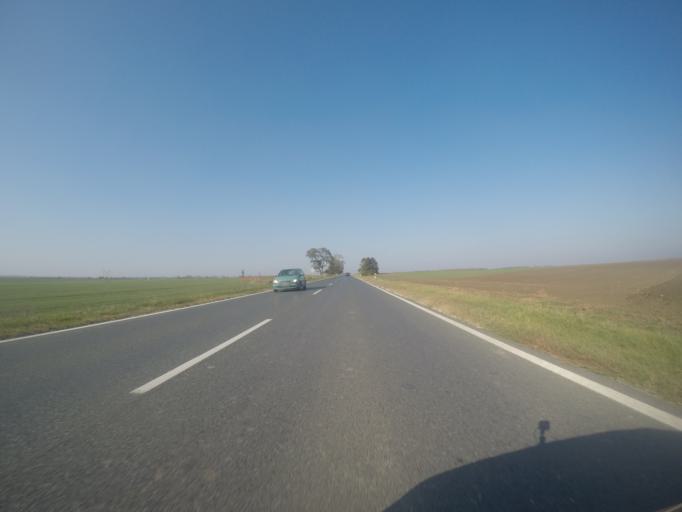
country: HU
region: Tolna
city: Madocsa
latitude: 46.7141
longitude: 18.8868
